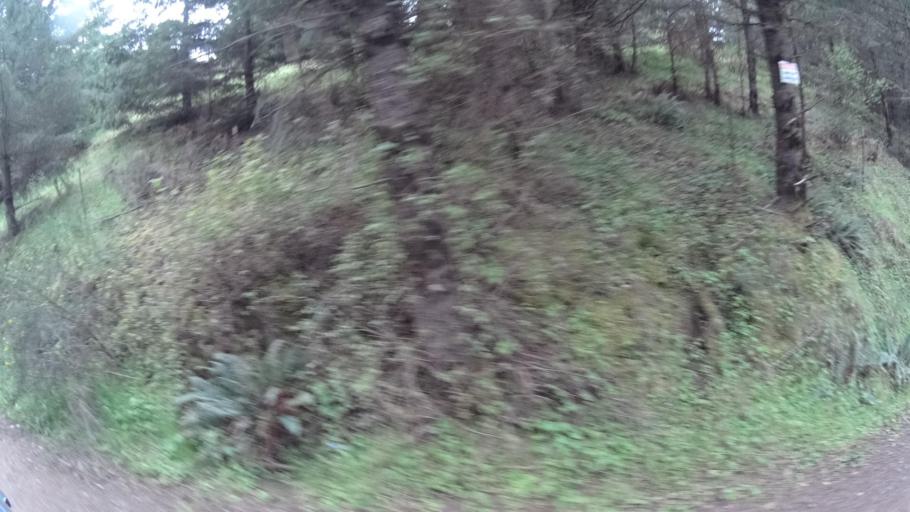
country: US
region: California
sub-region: Humboldt County
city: Redway
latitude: 40.2152
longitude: -123.7492
